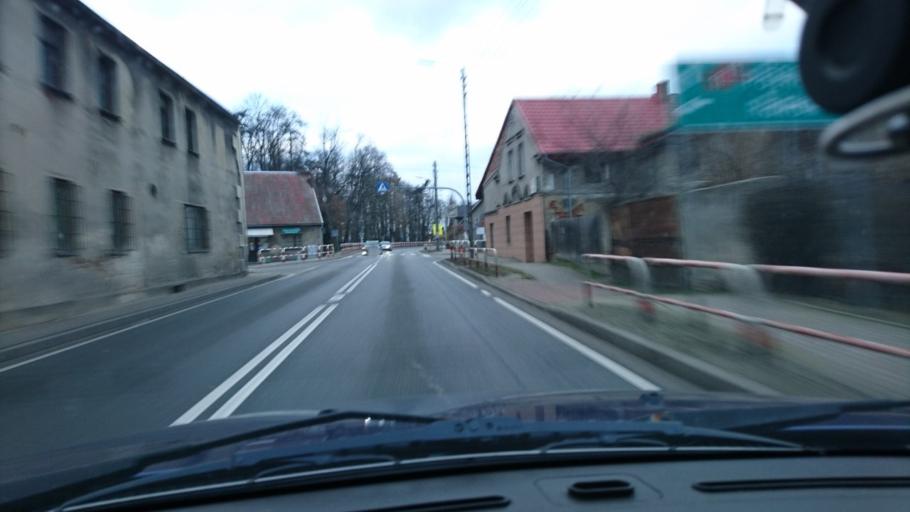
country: PL
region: Greater Poland Voivodeship
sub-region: Powiat kepinski
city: Opatow
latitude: 51.1792
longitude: 18.1434
